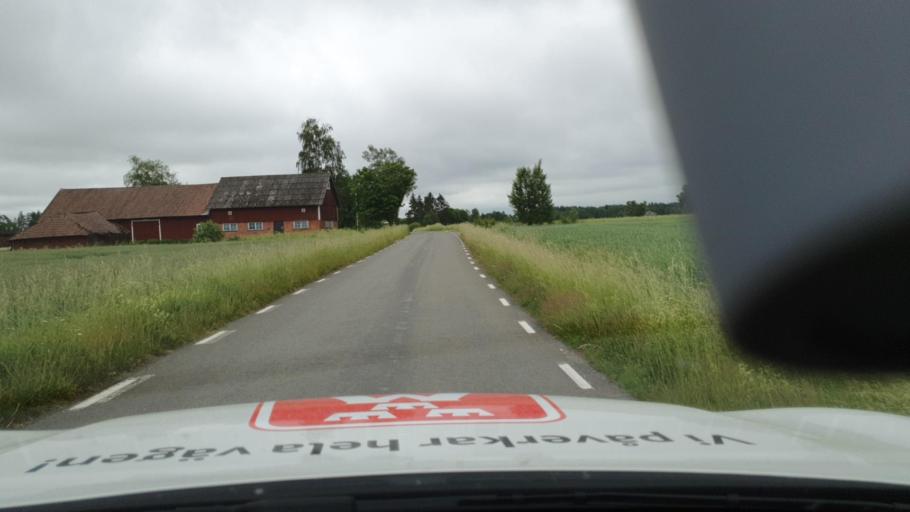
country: SE
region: Vaestra Goetaland
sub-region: Tidaholms Kommun
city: Olofstorp
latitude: 58.3761
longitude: 14.0054
